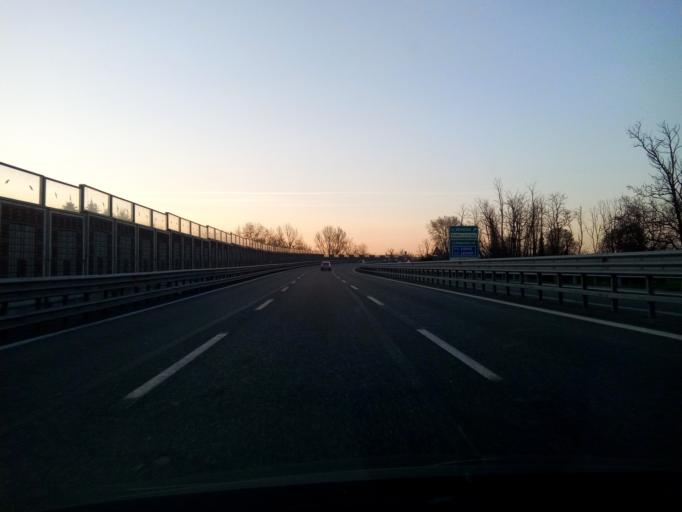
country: IT
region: Lombardy
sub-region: Citta metropolitana di Milano
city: Rho
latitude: 45.5153
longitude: 9.0612
